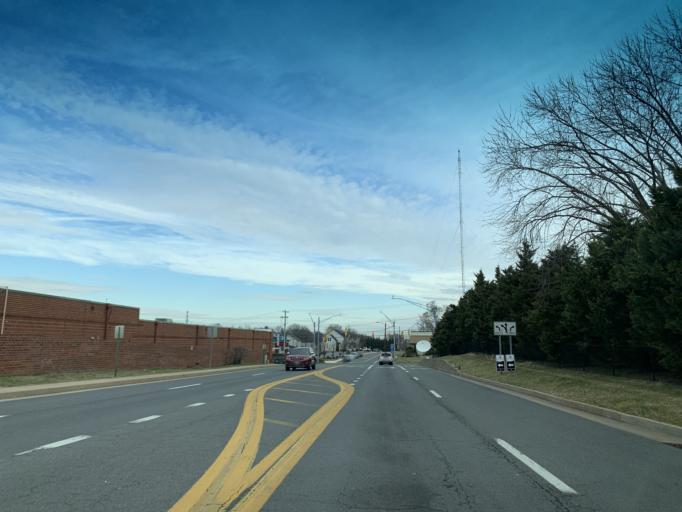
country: US
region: West Virginia
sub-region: Berkeley County
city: Martinsburg
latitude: 39.4621
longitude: -77.9871
